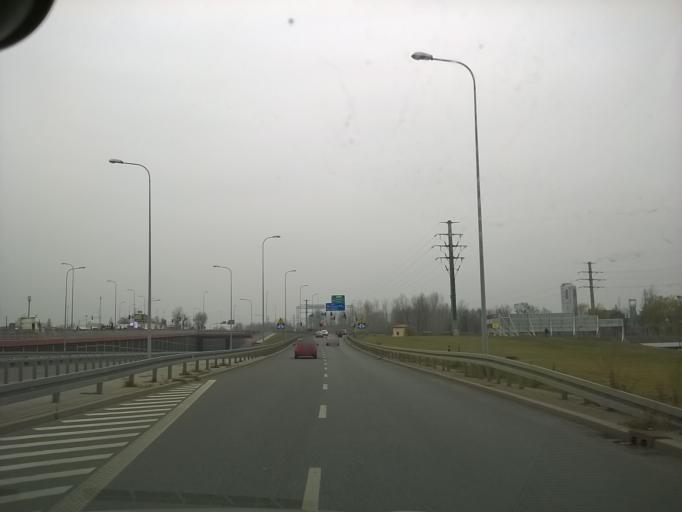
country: PL
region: Silesian Voivodeship
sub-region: Powiat gliwicki
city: Przyszowice
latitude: 50.2664
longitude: 18.7148
